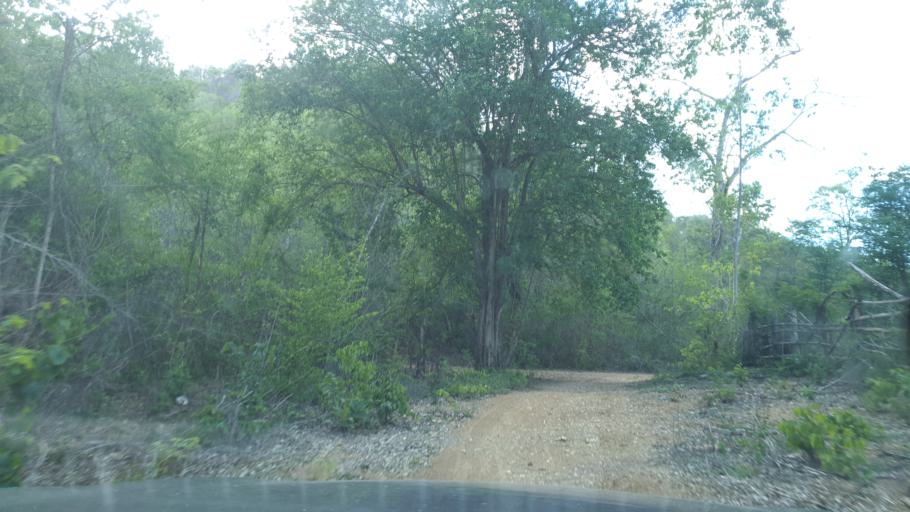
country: TH
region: Lampang
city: Sop Prap
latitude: 17.8415
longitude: 99.2868
